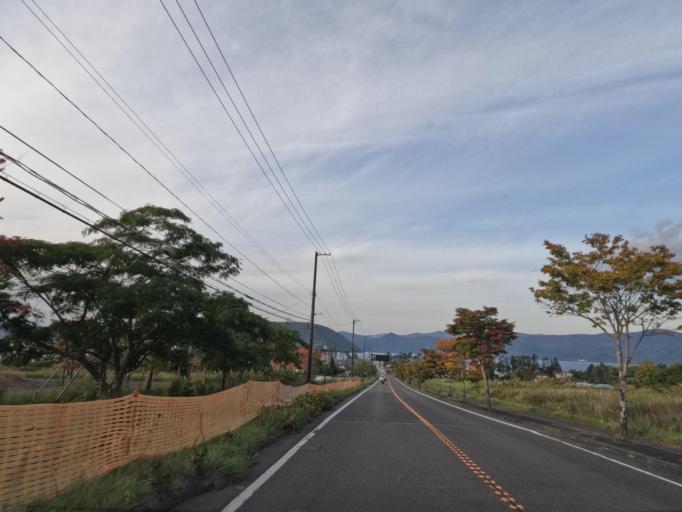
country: JP
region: Hokkaido
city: Date
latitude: 42.5535
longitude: 140.8623
